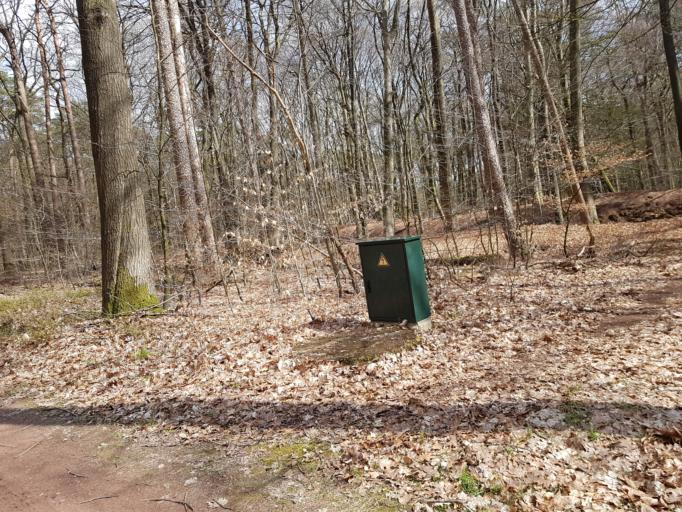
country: NL
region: Gelderland
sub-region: Gemeente Apeldoorn
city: Apeldoorn
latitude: 52.2448
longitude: 5.9260
